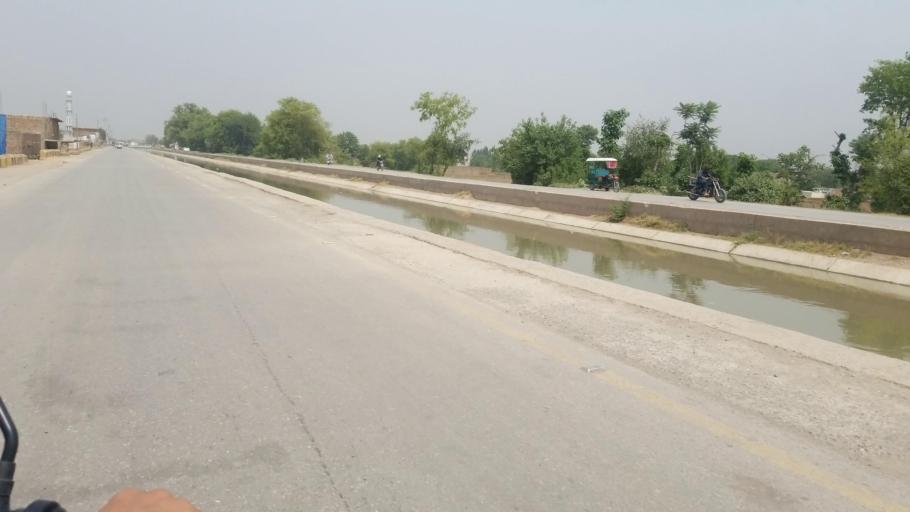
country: PK
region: Khyber Pakhtunkhwa
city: Peshawar
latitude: 33.9484
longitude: 71.5540
